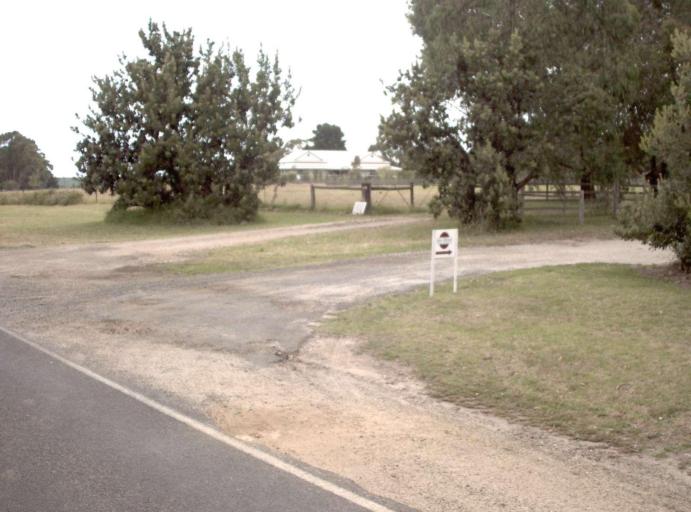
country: AU
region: Victoria
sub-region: Wellington
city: Sale
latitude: -38.1877
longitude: 147.0924
